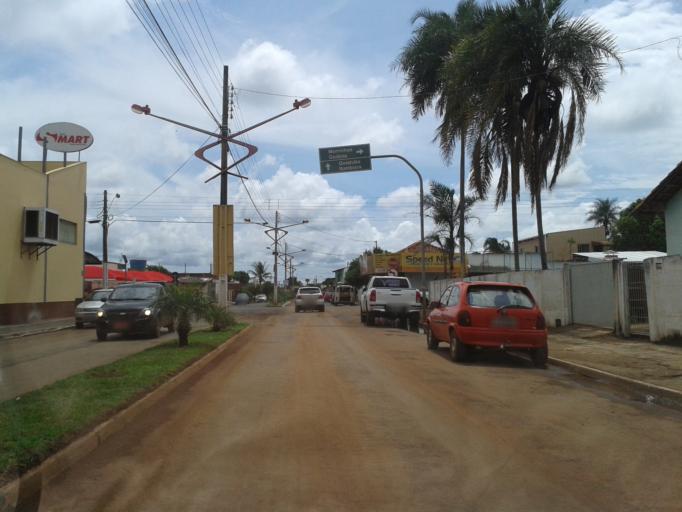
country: BR
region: Goias
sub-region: Buriti Alegre
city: Buriti Alegre
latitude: -18.1309
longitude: -49.0417
